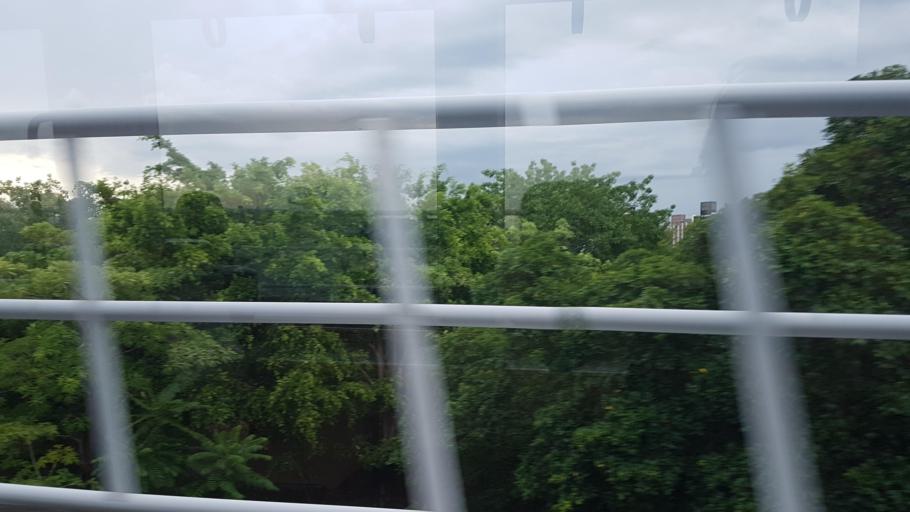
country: TW
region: Kaohsiung
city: Kaohsiung
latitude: 22.6178
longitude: 120.2874
